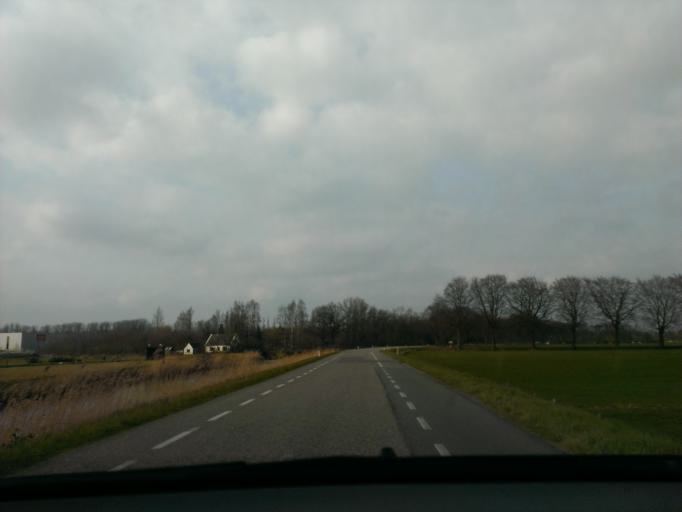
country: NL
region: Gelderland
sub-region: Gemeente Epe
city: Emst
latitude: 52.2987
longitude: 5.9998
